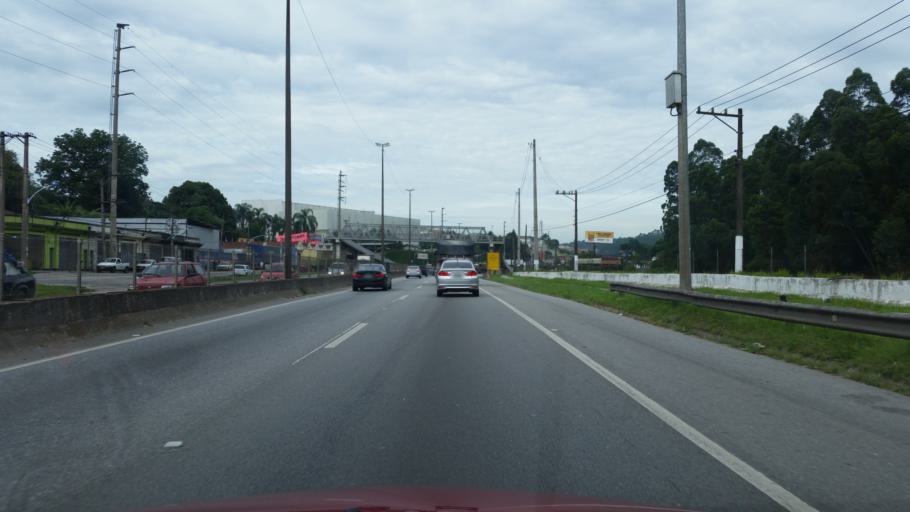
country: BR
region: Sao Paulo
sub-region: Taboao Da Serra
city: Taboao da Serra
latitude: -23.6175
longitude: -46.7955
